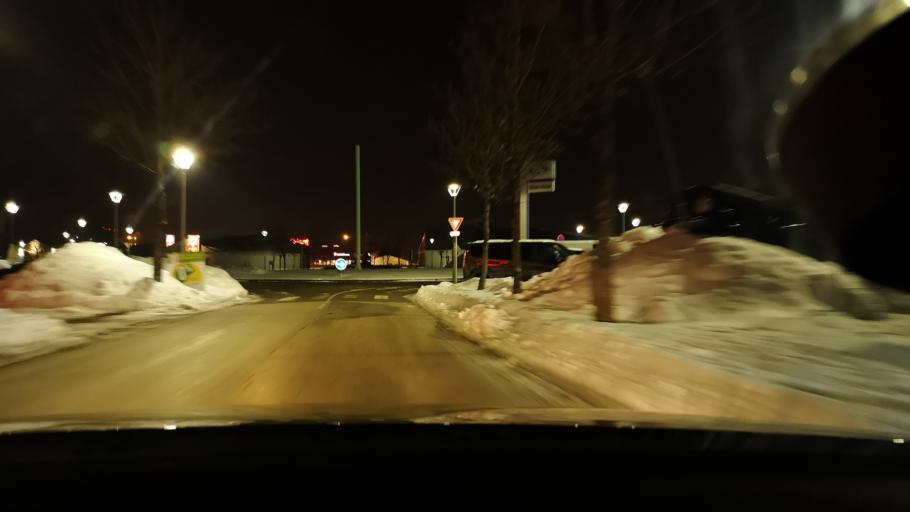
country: FR
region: Franche-Comte
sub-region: Departement du Doubs
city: Pontarlier
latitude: 46.9072
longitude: 6.3367
